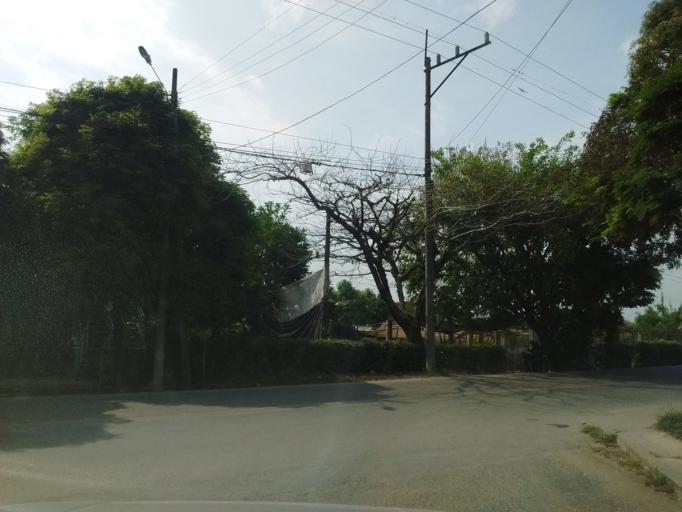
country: CO
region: Cauca
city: Puerto Tejada
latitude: 3.1707
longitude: -76.4574
